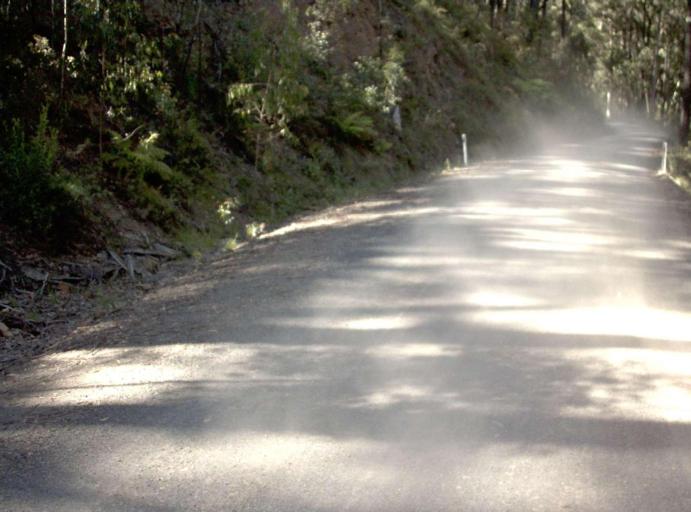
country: AU
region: New South Wales
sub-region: Bombala
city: Bombala
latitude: -37.2568
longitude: 148.7340
